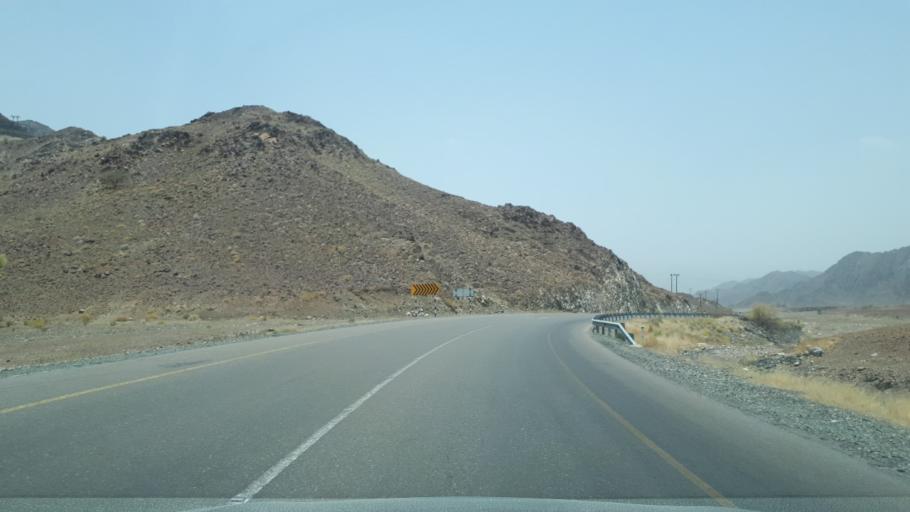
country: OM
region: Al Batinah
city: Rustaq
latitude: 23.4292
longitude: 57.2716
